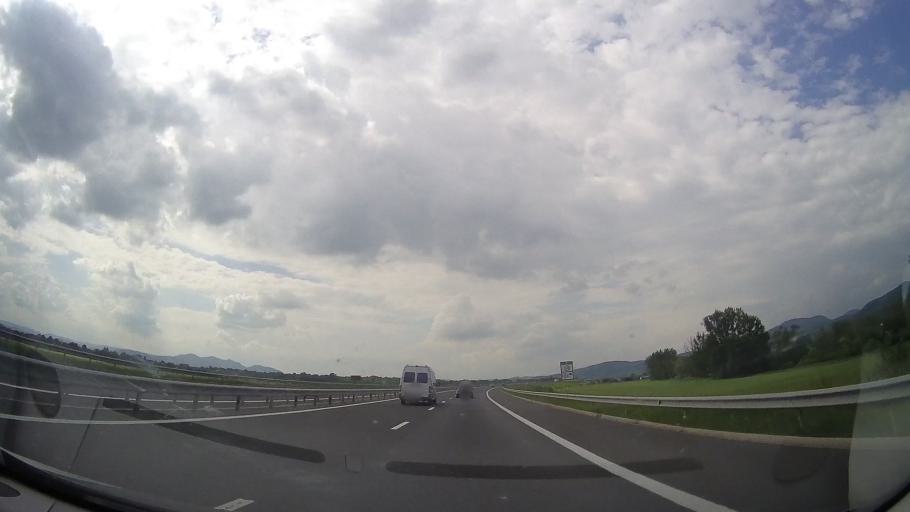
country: RO
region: Hunedoara
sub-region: Oras Simeria
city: Simeria
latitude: 45.8543
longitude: 23.0336
